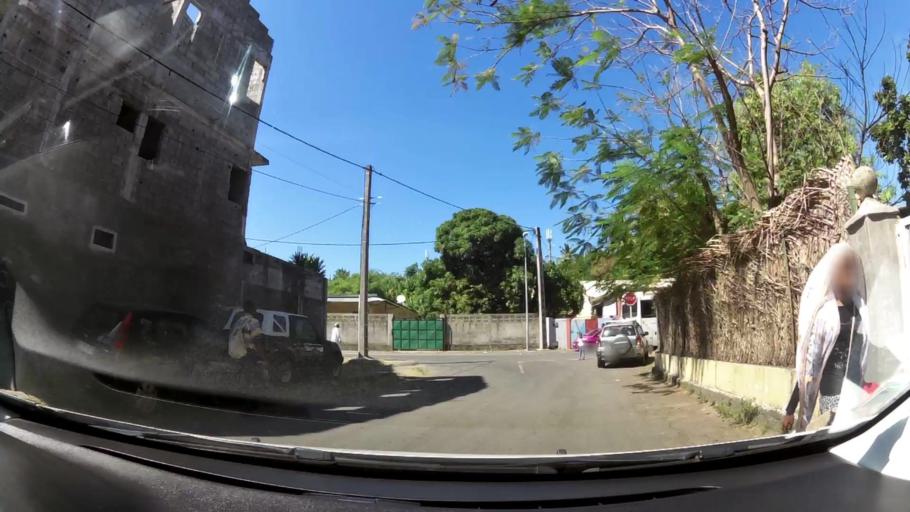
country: YT
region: Pamandzi
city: Pamandzi
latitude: -12.7971
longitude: 45.2783
